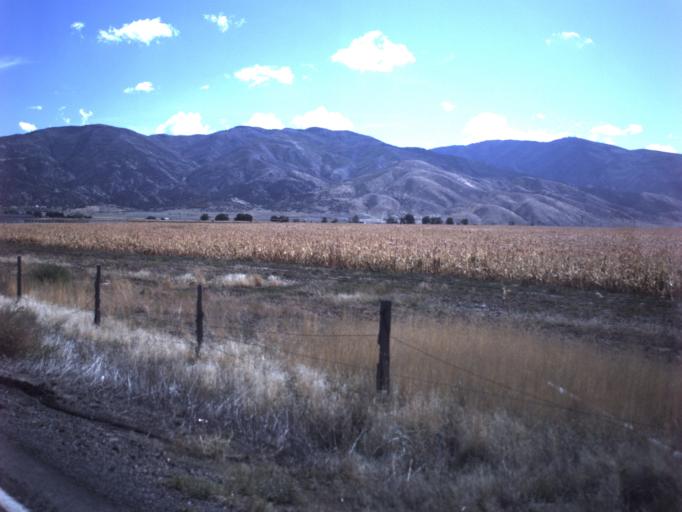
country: US
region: Utah
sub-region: Juab County
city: Nephi
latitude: 39.5580
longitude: -111.8964
